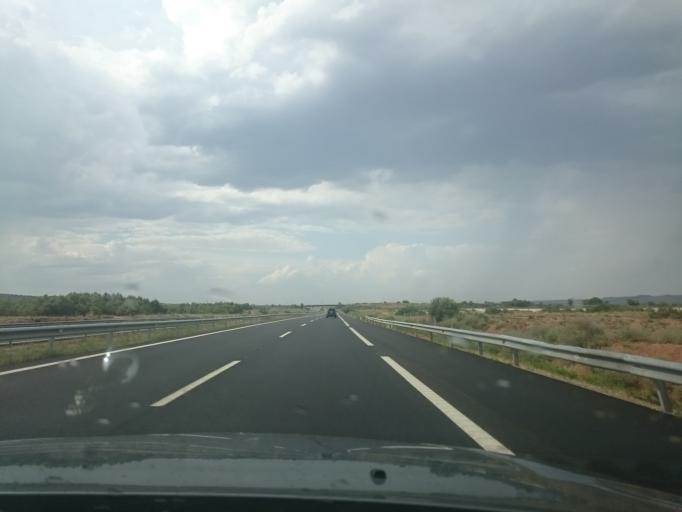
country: ES
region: Navarre
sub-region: Provincia de Navarra
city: Azagra
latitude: 42.2612
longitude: -1.9249
